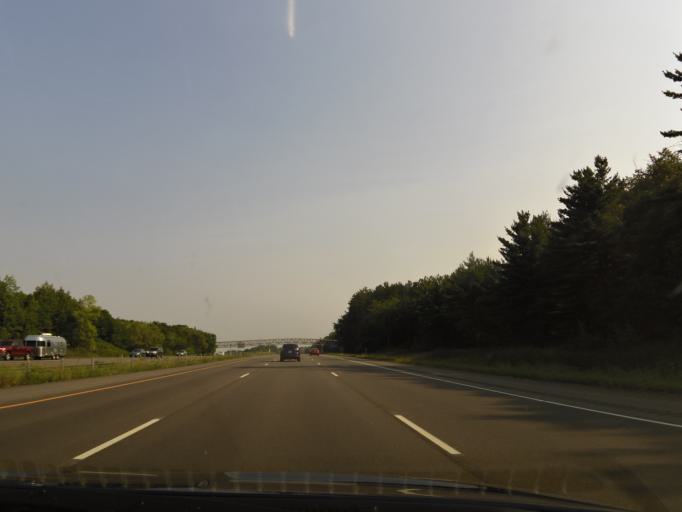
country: US
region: Minnesota
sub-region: Stearns County
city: Collegeville
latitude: 45.5920
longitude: -94.3733
